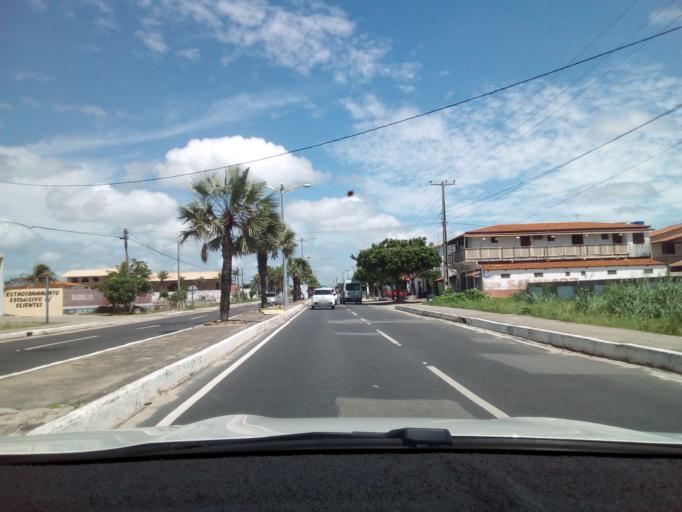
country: BR
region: Ceara
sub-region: Beberibe
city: Beberibe
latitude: -4.1823
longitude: -38.1364
